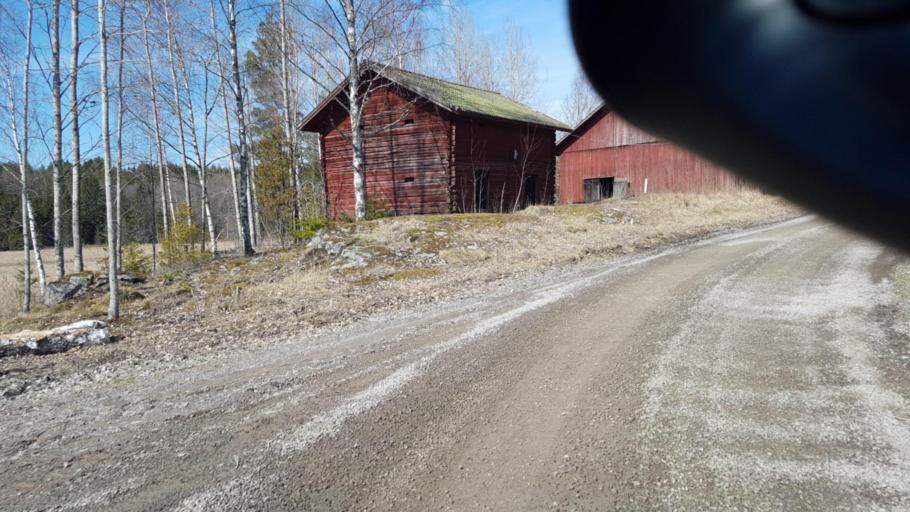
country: SE
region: Vaermland
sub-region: Grums Kommun
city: Grums
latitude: 59.4881
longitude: 12.9296
